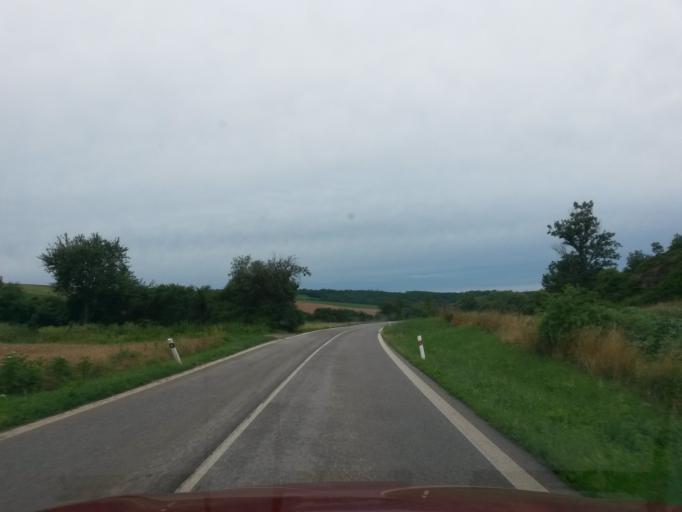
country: SK
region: Banskobystricky
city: Dudince
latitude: 48.1525
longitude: 18.9520
